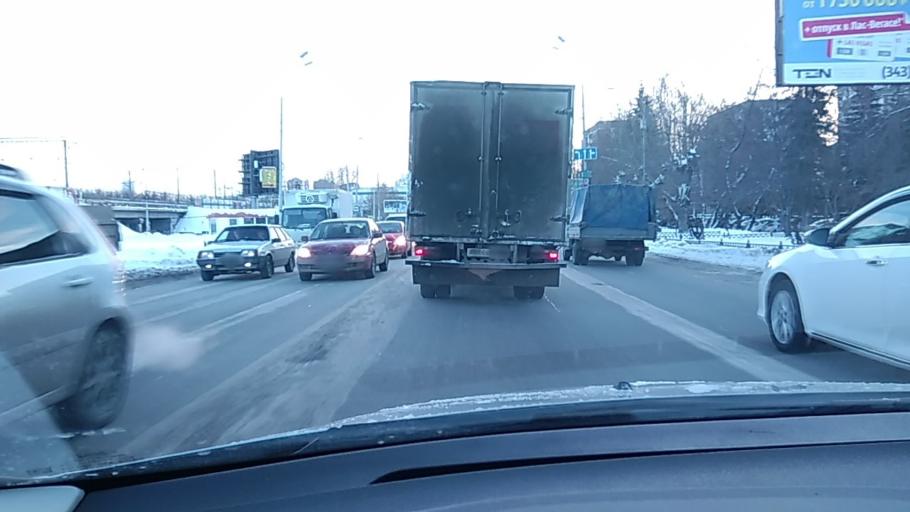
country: RU
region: Sverdlovsk
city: Yekaterinburg
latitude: 56.8389
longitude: 60.6329
